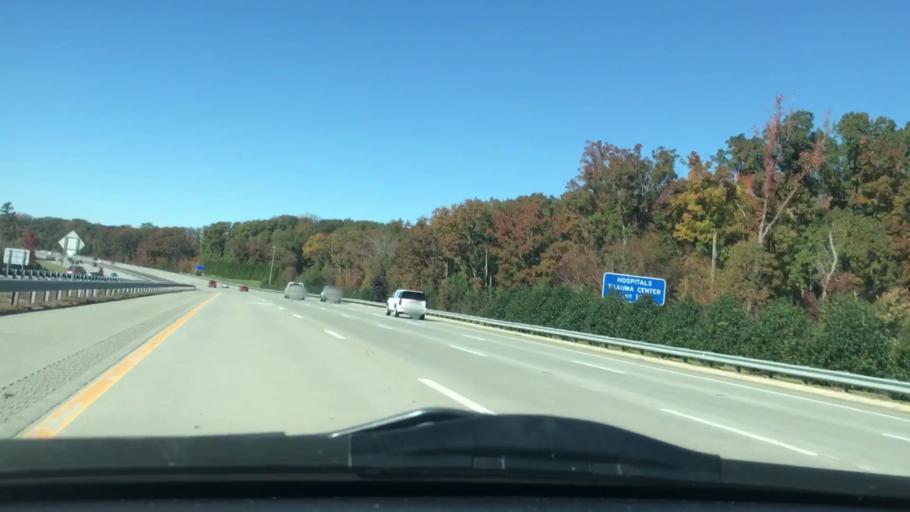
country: US
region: North Carolina
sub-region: Guilford County
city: Jamestown
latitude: 36.0379
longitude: -79.8908
